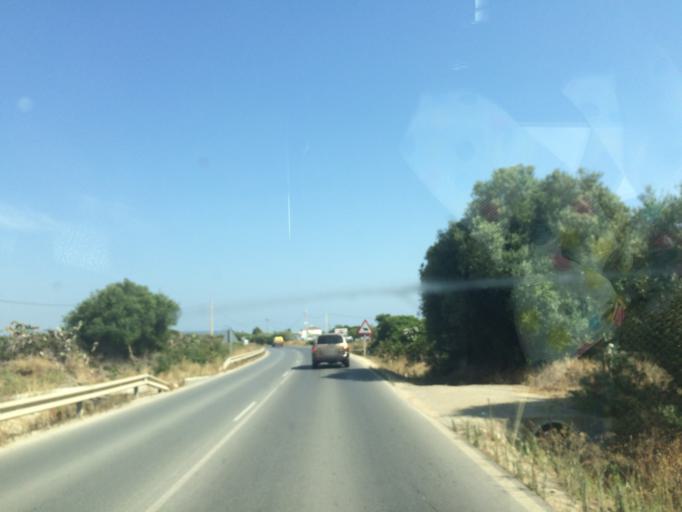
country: ES
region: Andalusia
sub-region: Provincia de Cadiz
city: Conil de la Frontera
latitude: 36.2454
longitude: -6.0640
